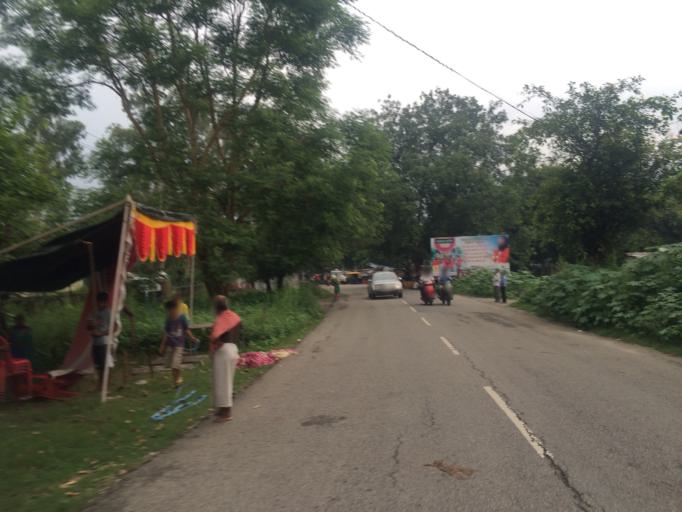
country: IN
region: Uttarakhand
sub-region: Dehradun
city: Birbhaddar
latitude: 30.0737
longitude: 78.2841
